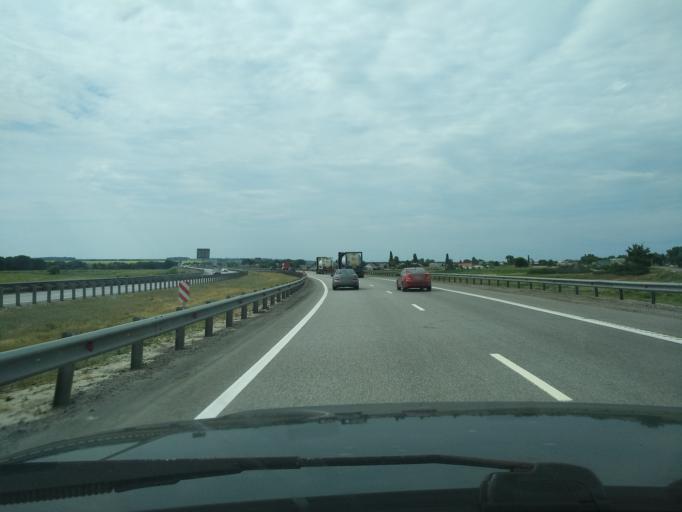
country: RU
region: Lipetsk
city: Khlevnoye
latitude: 52.0559
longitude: 39.1924
